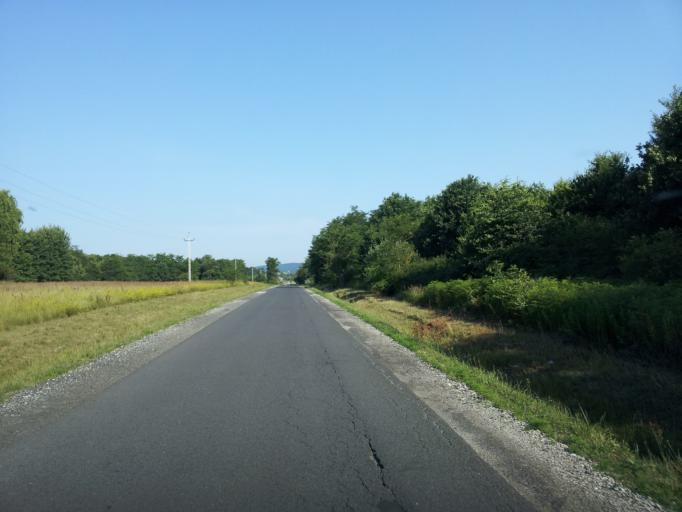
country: HU
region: Zala
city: Cserszegtomaj
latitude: 46.8672
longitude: 17.2720
